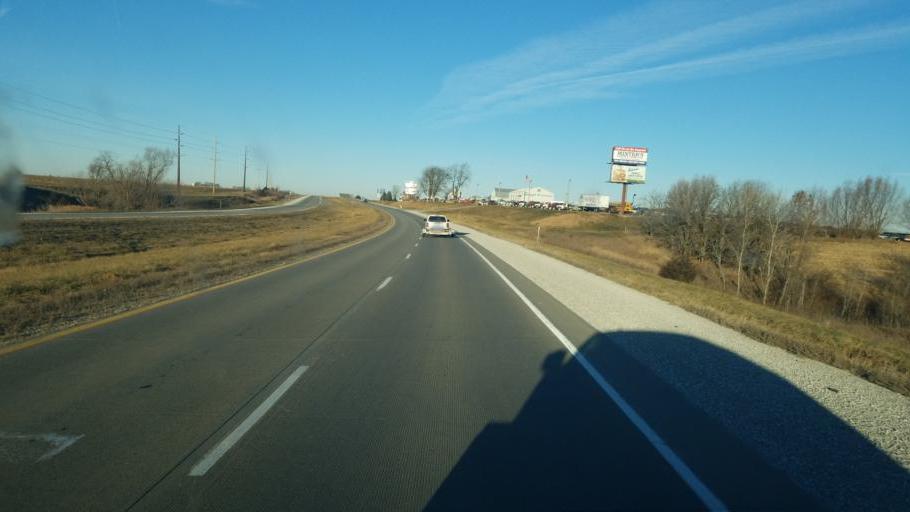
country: US
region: Iowa
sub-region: Marion County
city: Pella
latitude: 41.3873
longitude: -92.8280
